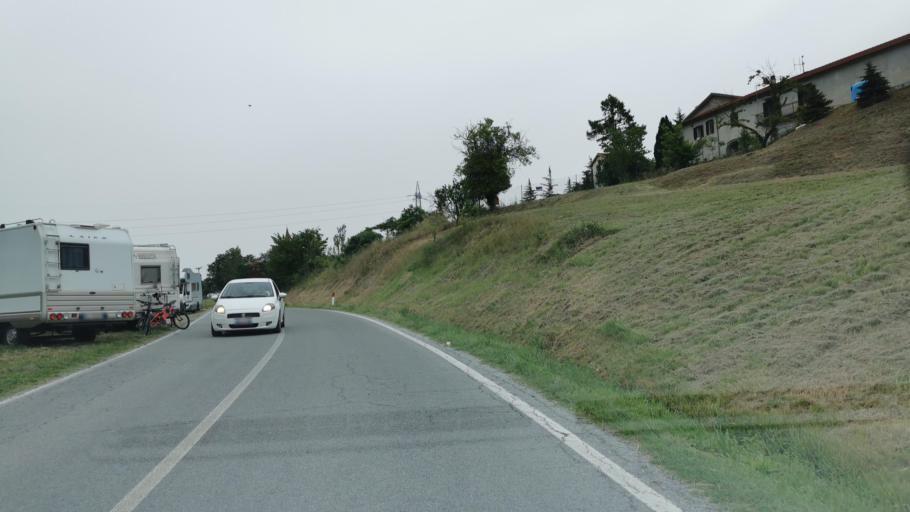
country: IT
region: Piedmont
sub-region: Provincia di Cuneo
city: Sale San Giovanni
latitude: 44.4015
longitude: 8.0771
